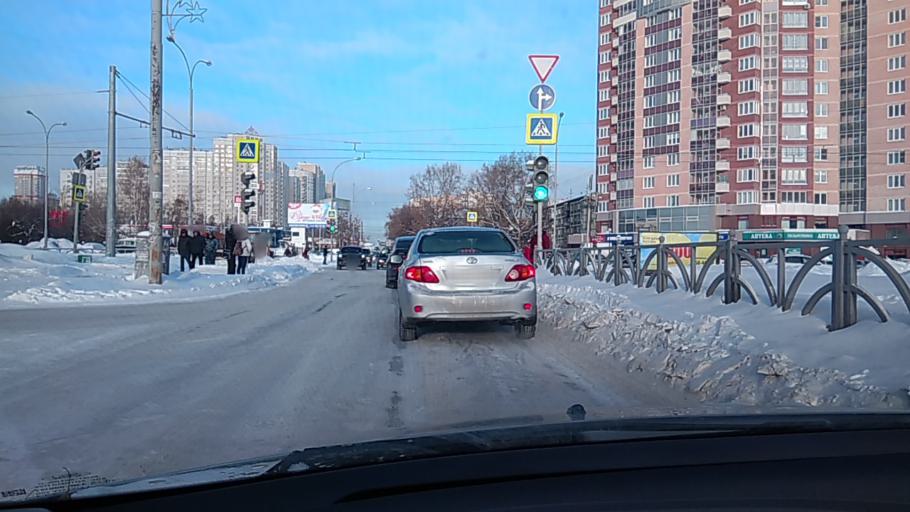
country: RU
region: Sverdlovsk
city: Yekaterinburg
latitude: 56.7973
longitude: 60.6142
